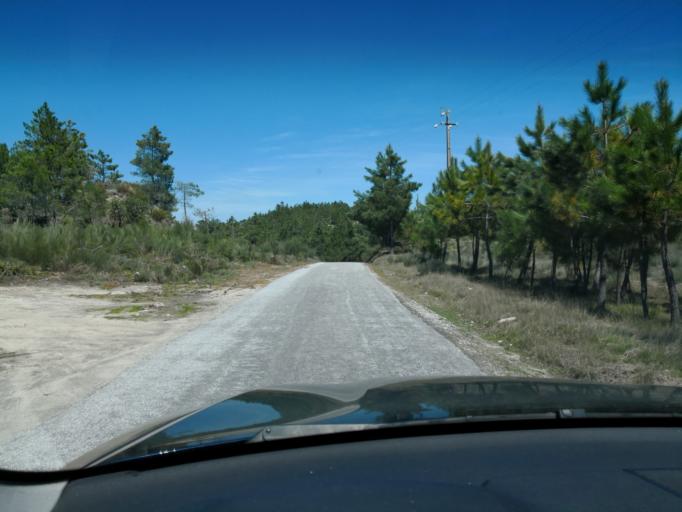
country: PT
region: Vila Real
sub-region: Vila Real
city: Vila Real
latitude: 41.3290
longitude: -7.6520
